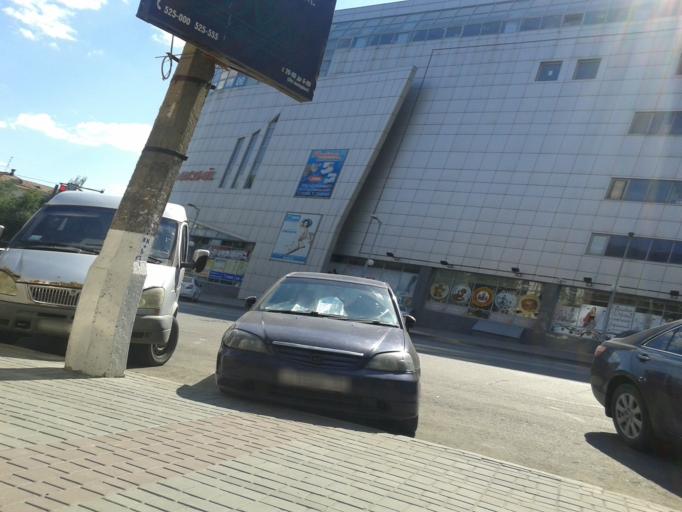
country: RU
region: Volgograd
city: Volgograd
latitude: 48.7080
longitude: 44.5223
